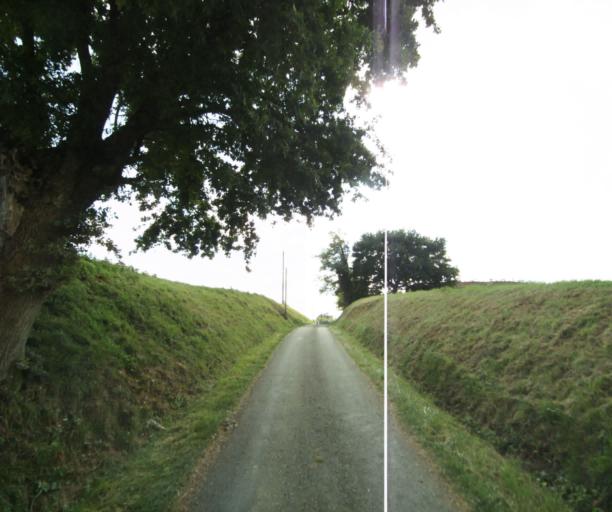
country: FR
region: Midi-Pyrenees
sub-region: Departement du Gers
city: Cazaubon
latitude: 43.9299
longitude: -0.0452
